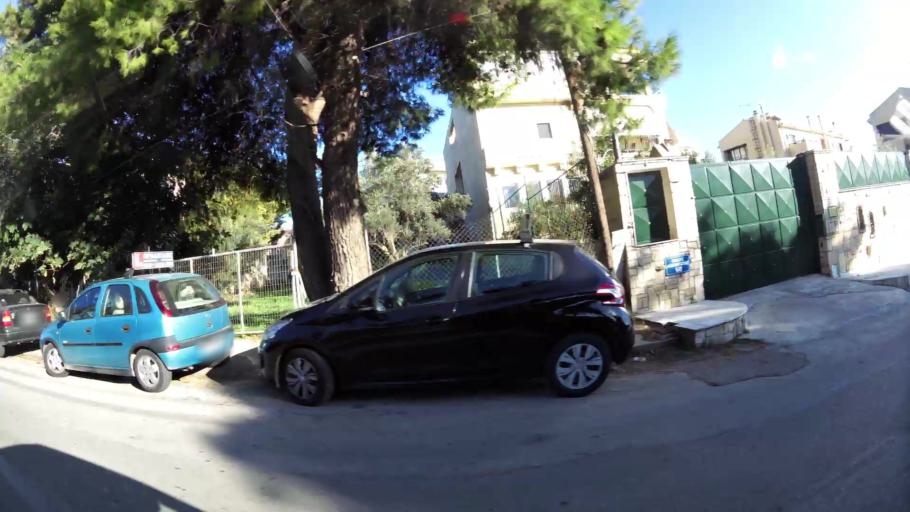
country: GR
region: Attica
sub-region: Nomarchia Anatolikis Attikis
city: Rafina
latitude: 38.0274
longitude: 23.9979
